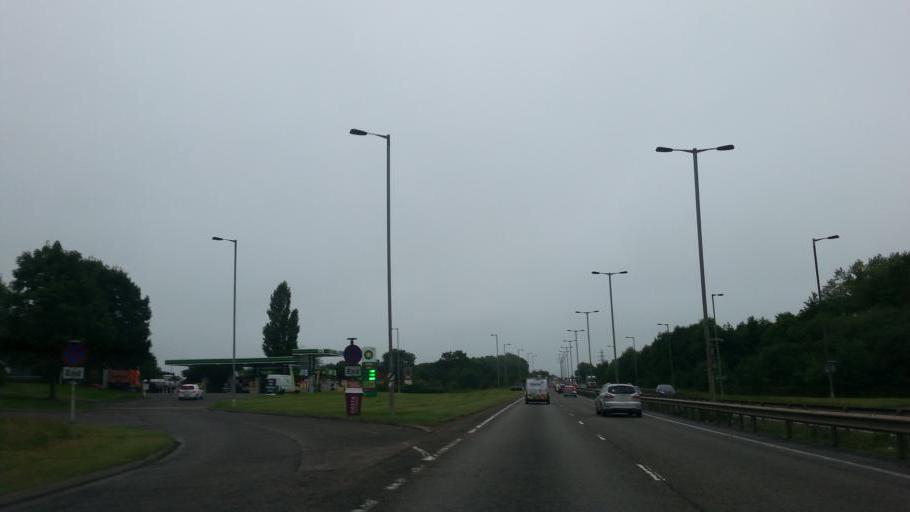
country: GB
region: England
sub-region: Warwickshire
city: Ryton on Dunsmore
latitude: 52.3899
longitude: -1.4387
